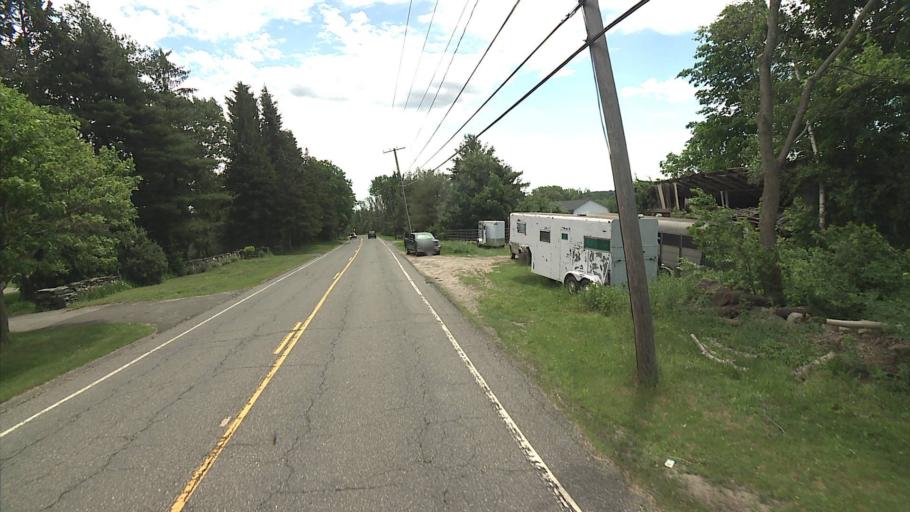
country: US
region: Connecticut
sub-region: Litchfield County
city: Litchfield
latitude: 41.6930
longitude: -73.1824
